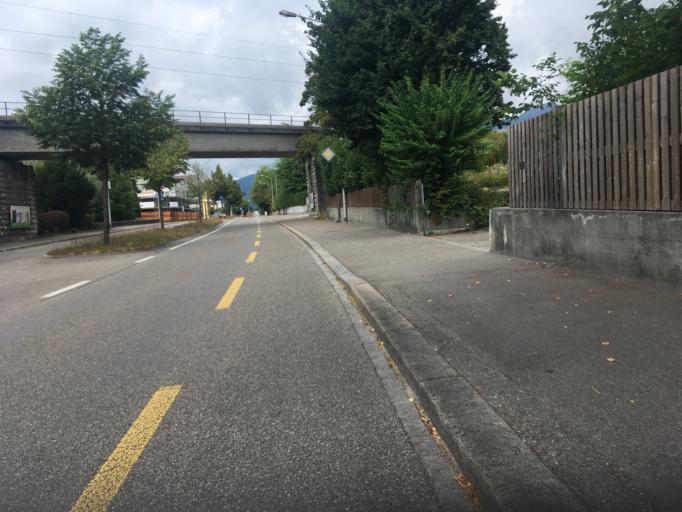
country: CH
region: Solothurn
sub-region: Bezirk Lebern
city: Langendorf
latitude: 47.2122
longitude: 7.5220
